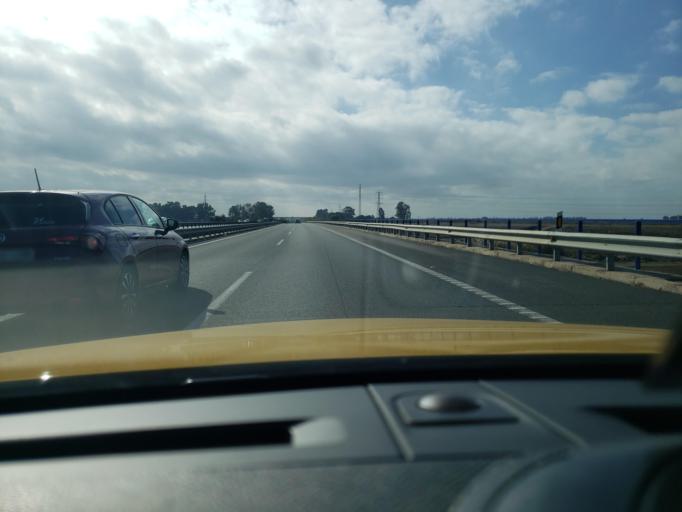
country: ES
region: Andalusia
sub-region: Provincia de Sevilla
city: Los Palacios y Villafranca
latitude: 37.1501
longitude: -5.9138
